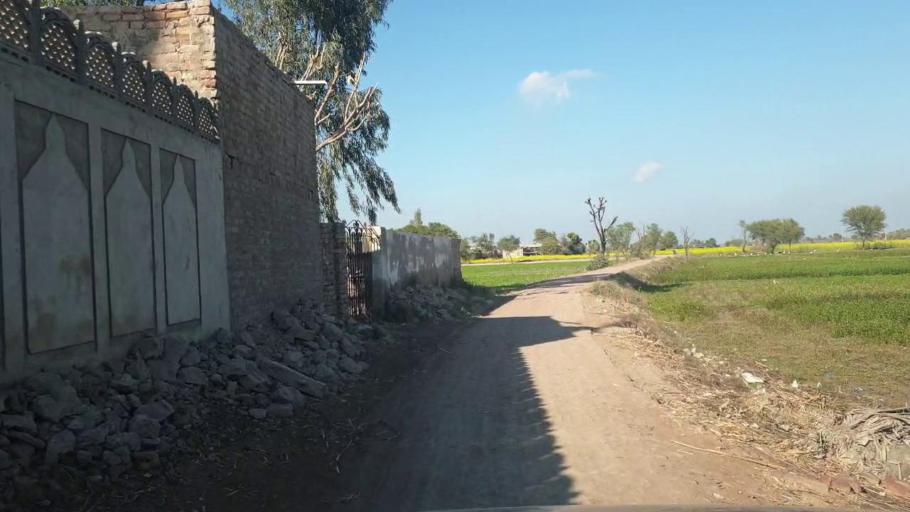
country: PK
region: Sindh
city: Shahdadpur
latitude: 25.9359
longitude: 68.5216
